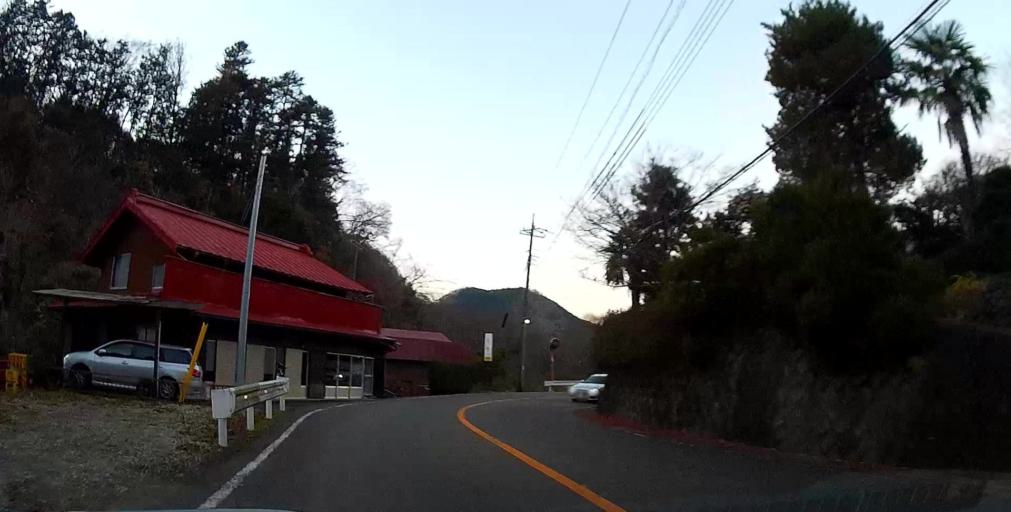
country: JP
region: Yamanashi
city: Uenohara
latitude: 35.5875
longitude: 139.1730
